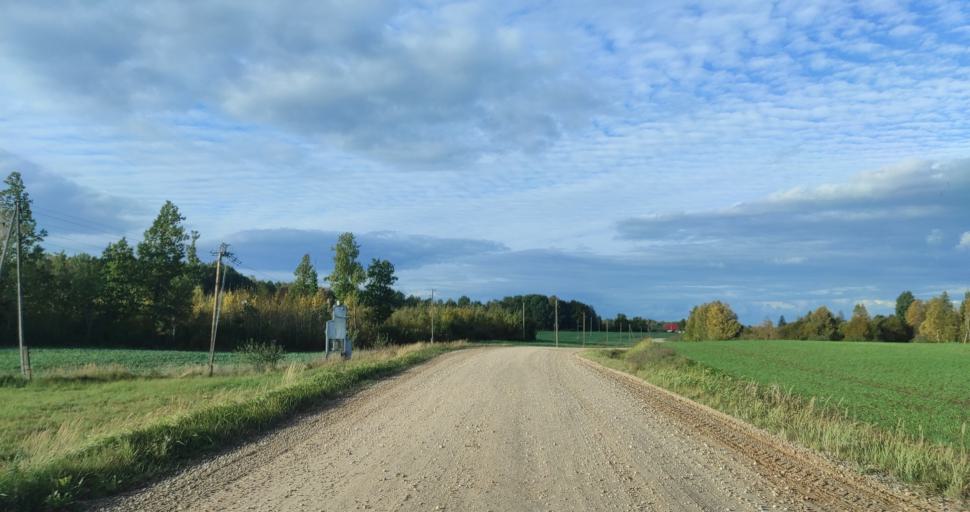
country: LV
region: Skrunda
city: Skrunda
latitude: 56.7473
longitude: 21.8197
